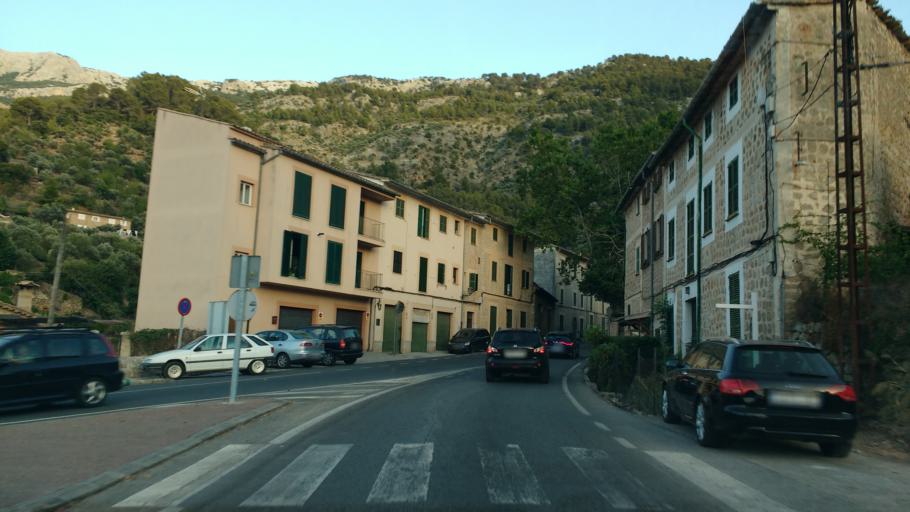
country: ES
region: Balearic Islands
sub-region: Illes Balears
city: Soller
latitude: 39.7607
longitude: 2.7113
